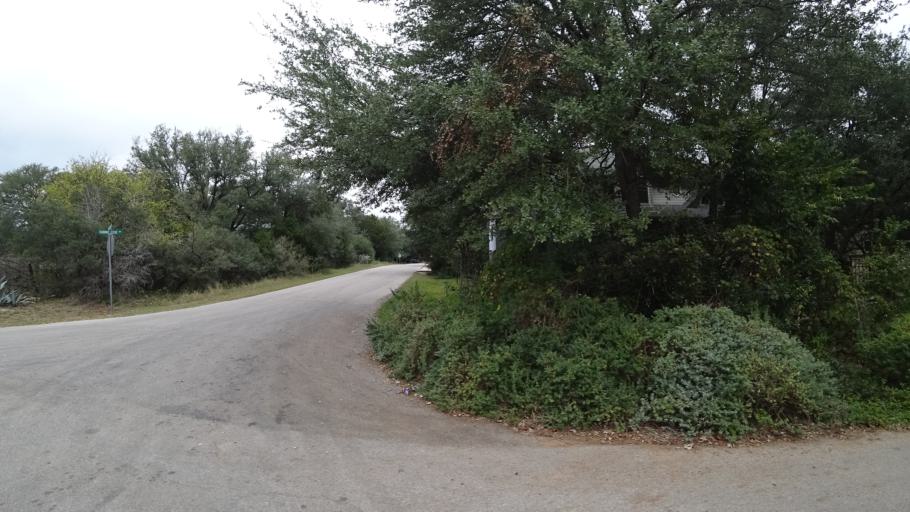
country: US
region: Texas
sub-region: Travis County
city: Bee Cave
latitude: 30.3290
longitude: -97.9236
